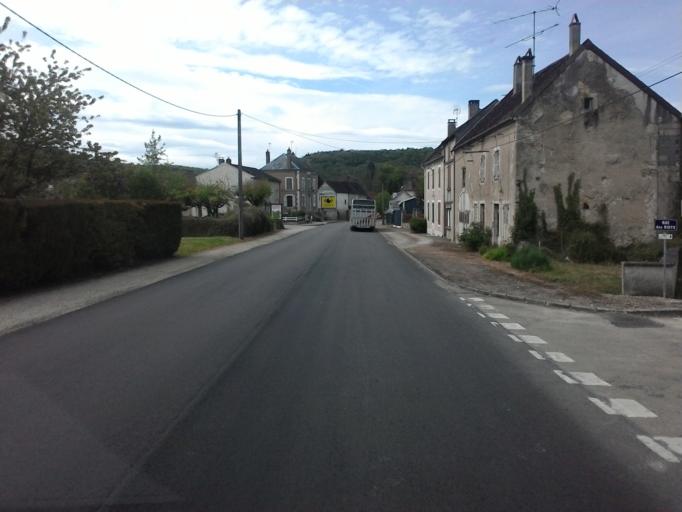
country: FR
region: Bourgogne
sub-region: Departement de l'Yonne
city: Joux-la-Ville
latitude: 47.5614
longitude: 3.7860
